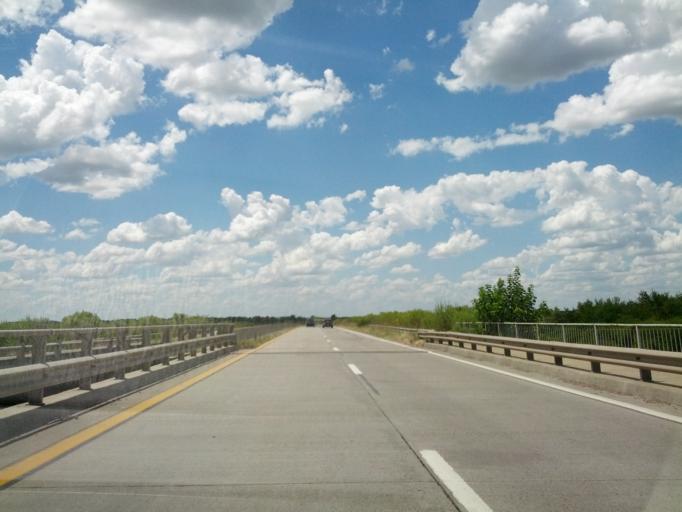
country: AR
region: Entre Rios
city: Gualeguaychu
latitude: -32.9550
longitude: -58.5819
